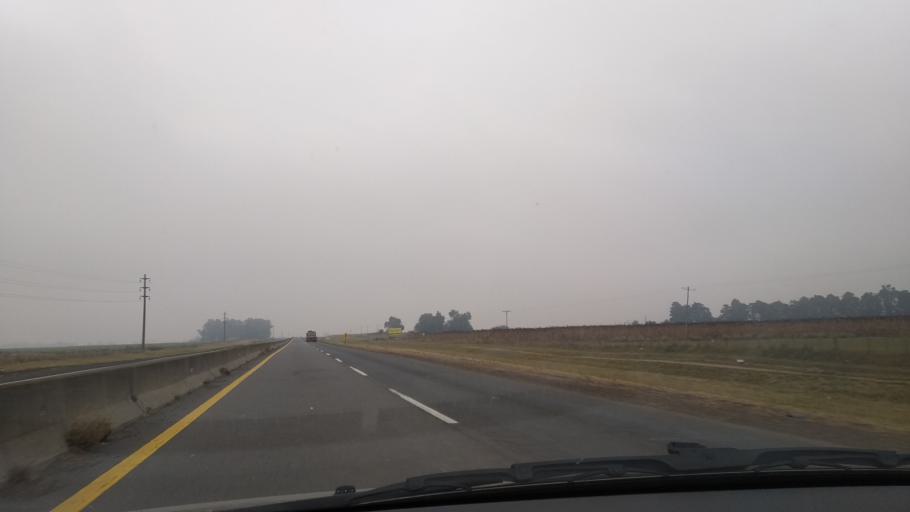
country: AR
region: Buenos Aires
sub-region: Partido de Azul
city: Azul
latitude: -36.8558
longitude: -60.0554
